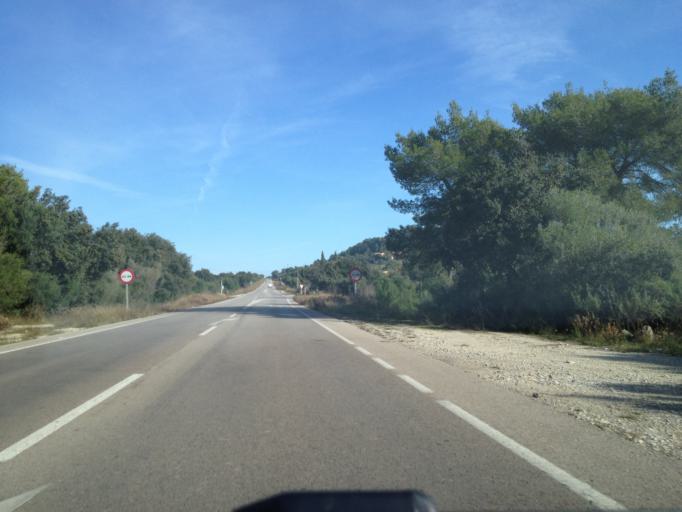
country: ES
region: Balearic Islands
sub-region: Illes Balears
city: Capdepera
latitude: 39.6828
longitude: 3.4130
